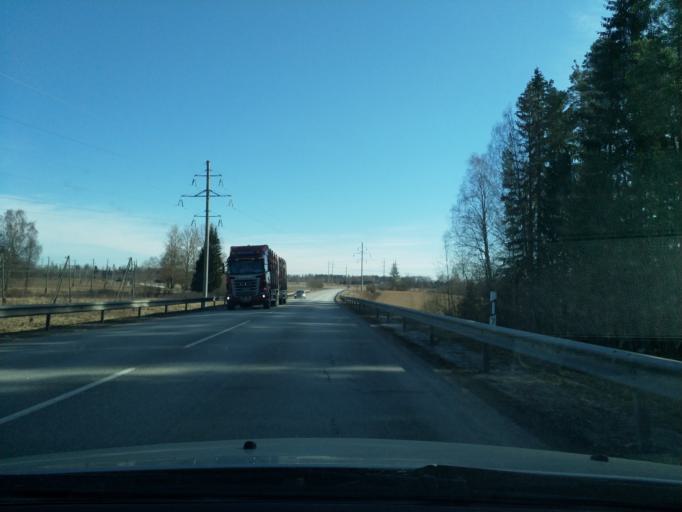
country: LV
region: Valmieras Rajons
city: Valmiera
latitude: 57.5102
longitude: 25.4420
